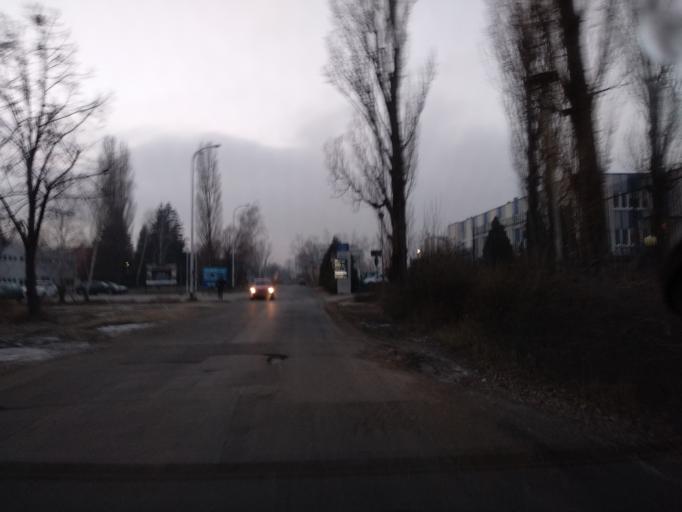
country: PL
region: Lower Silesian Voivodeship
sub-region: Powiat wroclawski
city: Wroclaw
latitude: 51.1125
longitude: 16.9826
